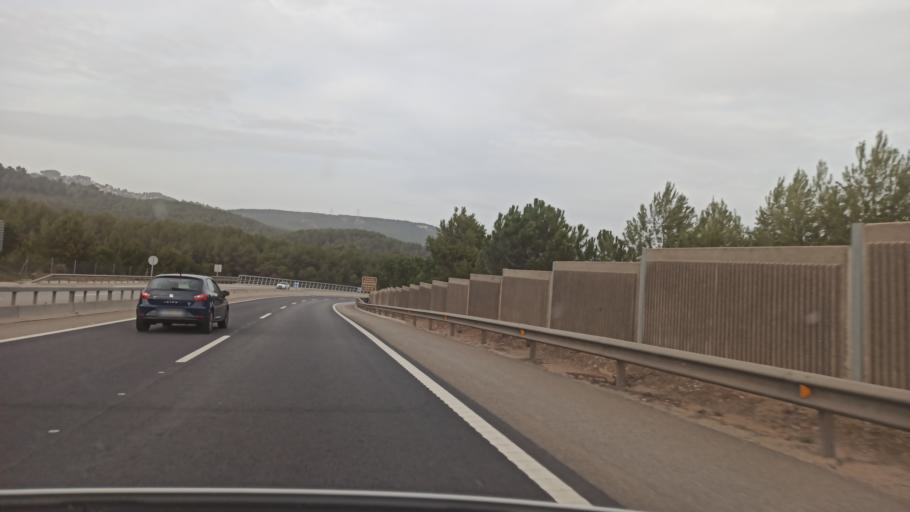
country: ES
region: Catalonia
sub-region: Provincia de Barcelona
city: Cervello
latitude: 41.3929
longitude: 1.9673
